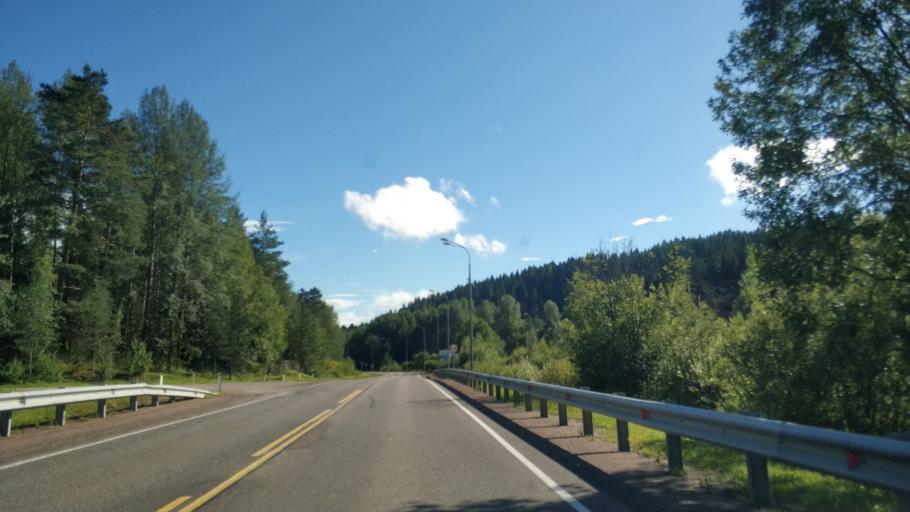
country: RU
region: Republic of Karelia
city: Sortavala
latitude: 61.6684
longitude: 30.6539
